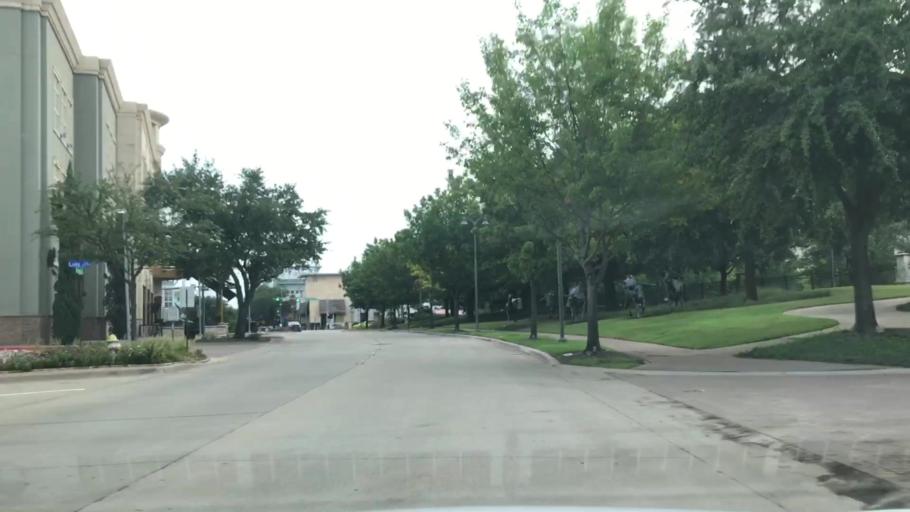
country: US
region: Texas
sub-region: Denton County
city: The Colony
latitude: 33.0792
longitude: -96.8213
